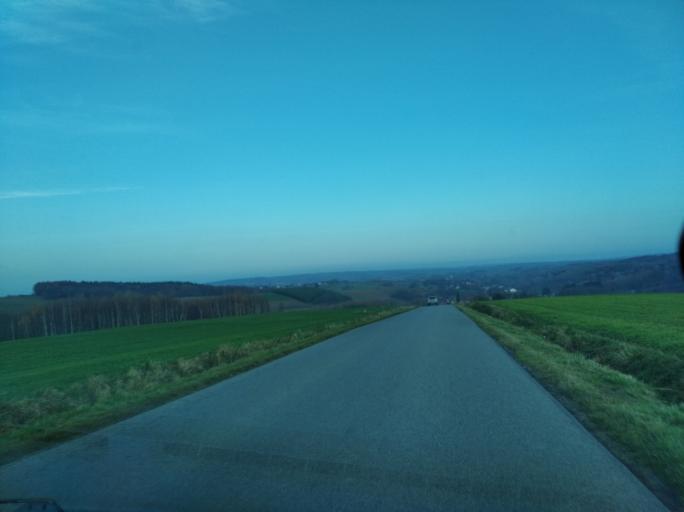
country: PL
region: Subcarpathian Voivodeship
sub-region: Powiat ropczycko-sedziszowski
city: Zagorzyce
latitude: 49.9870
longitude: 21.7198
